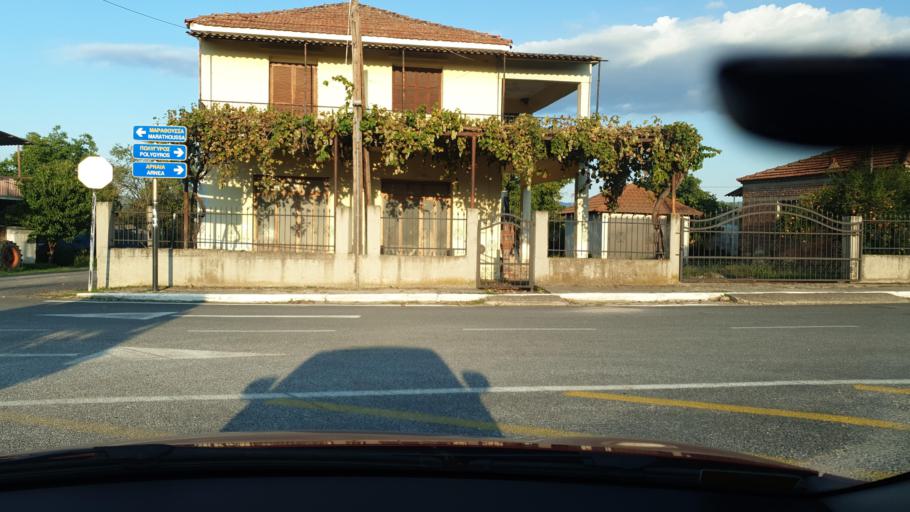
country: GR
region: Central Macedonia
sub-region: Nomos Thessalonikis
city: Nea Apollonia
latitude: 40.5470
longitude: 23.4484
